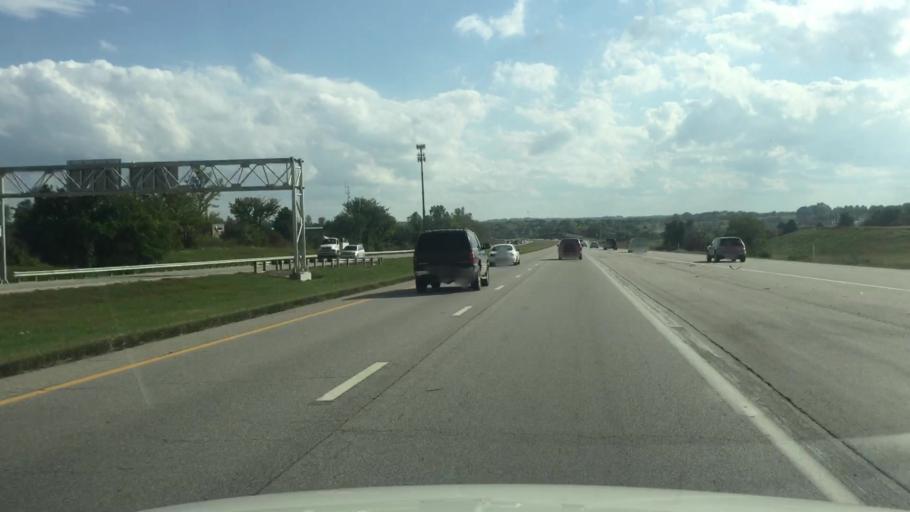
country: US
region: Kansas
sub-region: Johnson County
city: Lenexa
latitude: 38.8365
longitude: -94.6771
